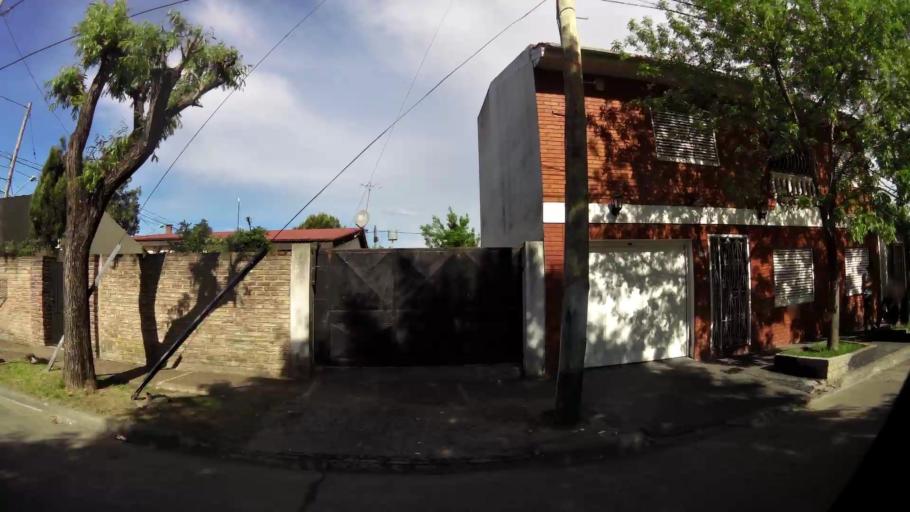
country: AR
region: Buenos Aires
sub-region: Partido de Almirante Brown
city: Adrogue
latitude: -34.8191
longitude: -58.3435
